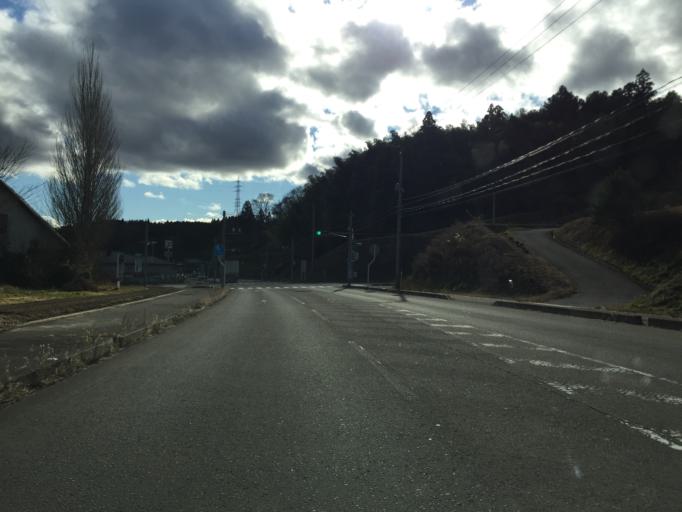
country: JP
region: Fukushima
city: Funehikimachi-funehiki
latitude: 37.5693
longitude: 140.5779
